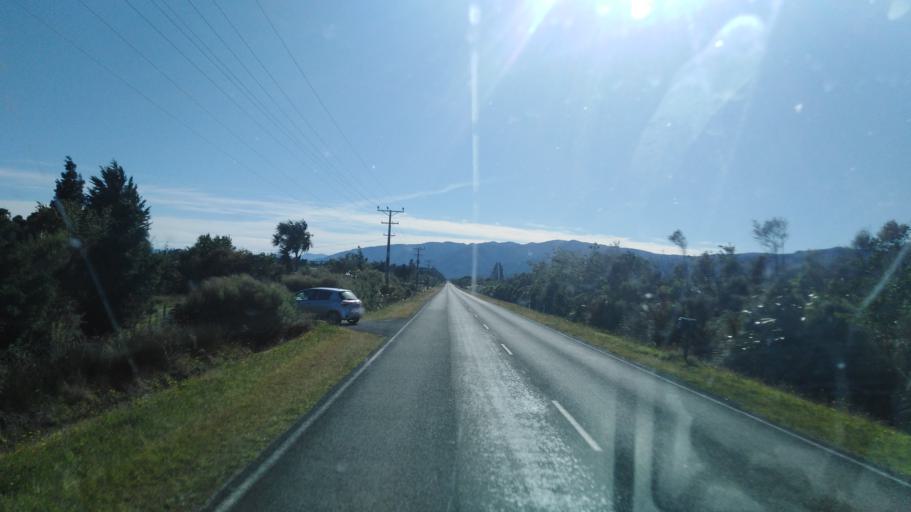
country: NZ
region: West Coast
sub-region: Buller District
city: Westport
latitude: -41.7481
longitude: 171.6785
